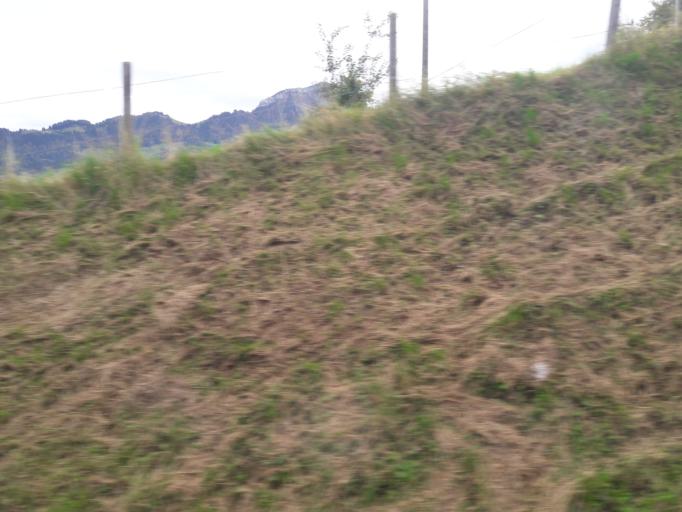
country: CH
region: Schwyz
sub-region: Bezirk Schwyz
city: Goldau
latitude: 47.0525
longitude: 8.5776
